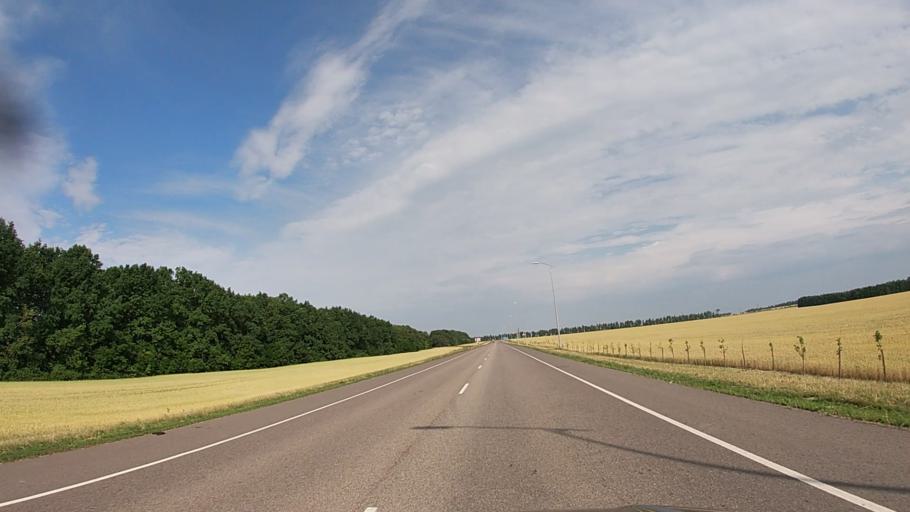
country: RU
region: Belgorod
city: Proletarskiy
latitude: 50.8267
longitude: 35.7782
